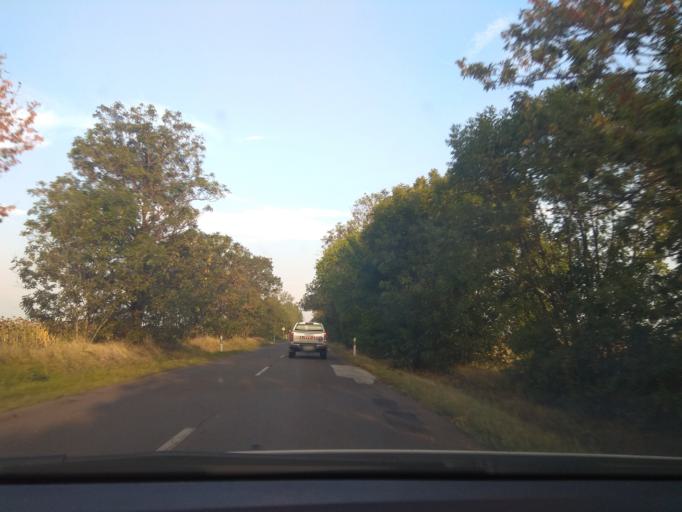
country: HU
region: Heves
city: Ostoros
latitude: 47.8289
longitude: 20.4582
